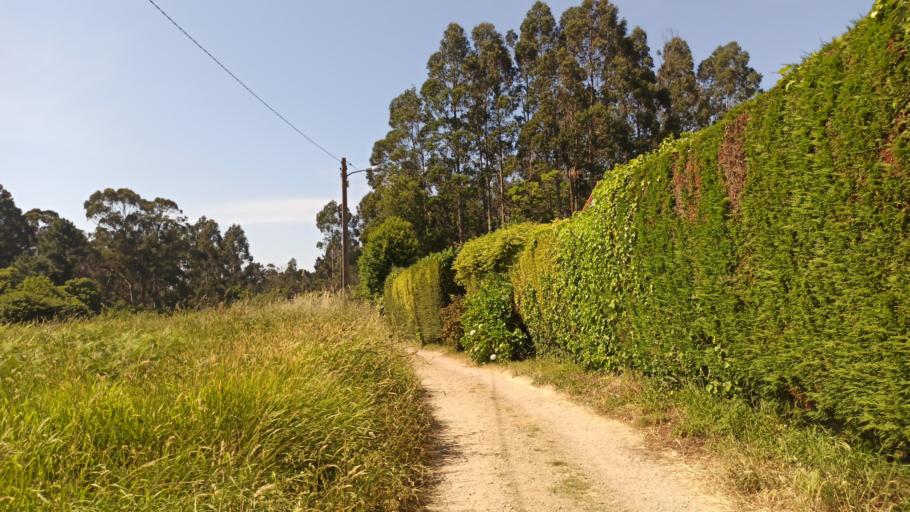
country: ES
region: Galicia
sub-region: Provincia da Coruna
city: Sada
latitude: 43.3788
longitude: -8.2698
